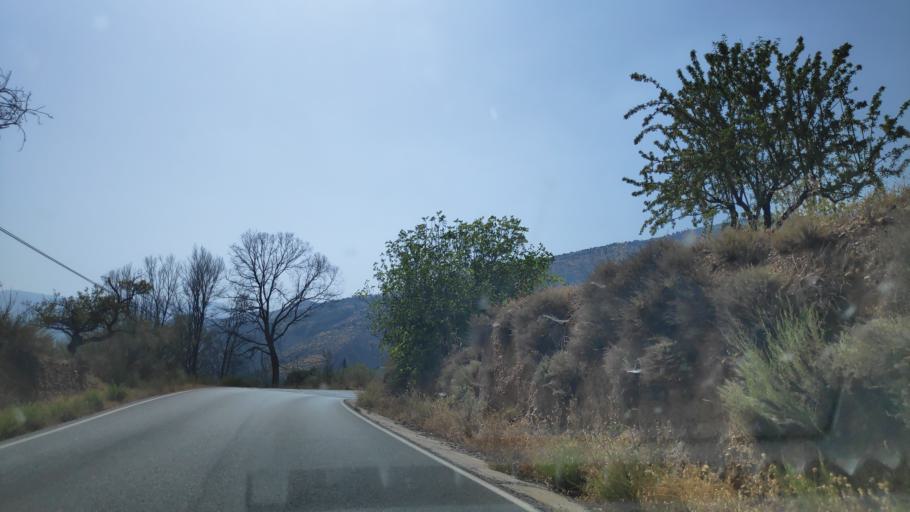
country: ES
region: Andalusia
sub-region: Provincia de Granada
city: Soportujar
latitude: 36.9241
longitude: -3.3965
